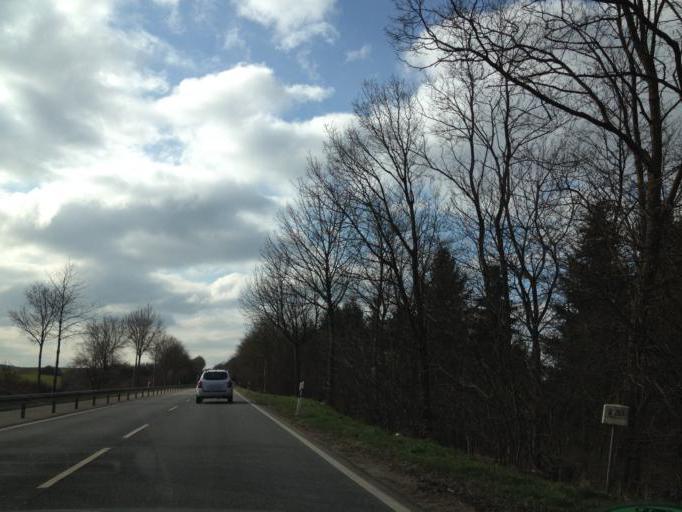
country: DE
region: Saarland
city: Sankt Wendel
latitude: 49.4691
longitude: 7.1363
